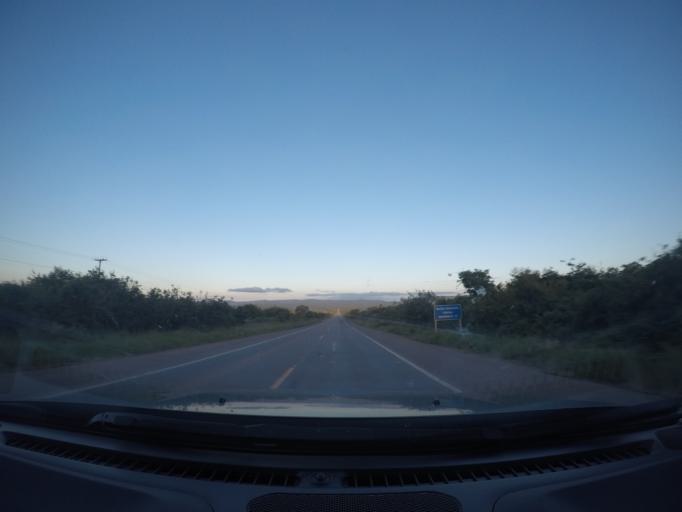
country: BR
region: Bahia
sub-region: Seabra
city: Seabra
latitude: -12.4101
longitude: -41.9687
